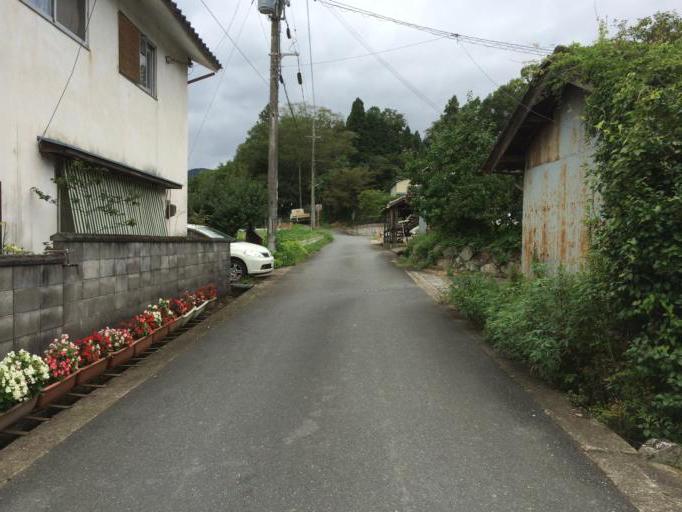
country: JP
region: Kyoto
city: Fukuchiyama
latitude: 35.2235
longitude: 135.1289
